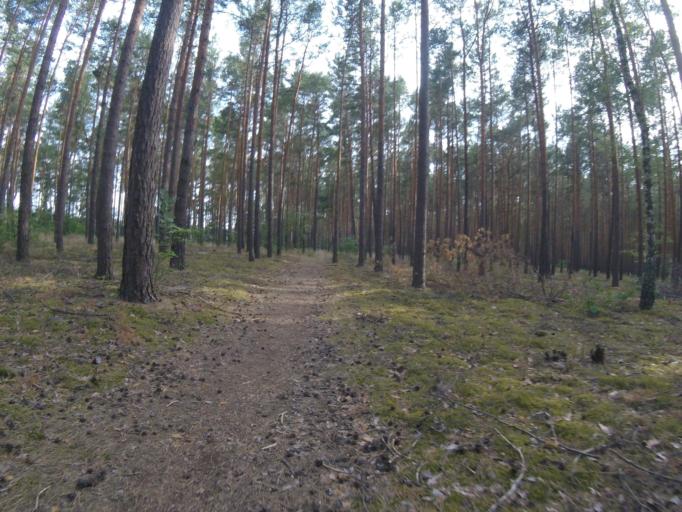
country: DE
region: Brandenburg
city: Gross Koris
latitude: 52.2090
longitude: 13.7427
